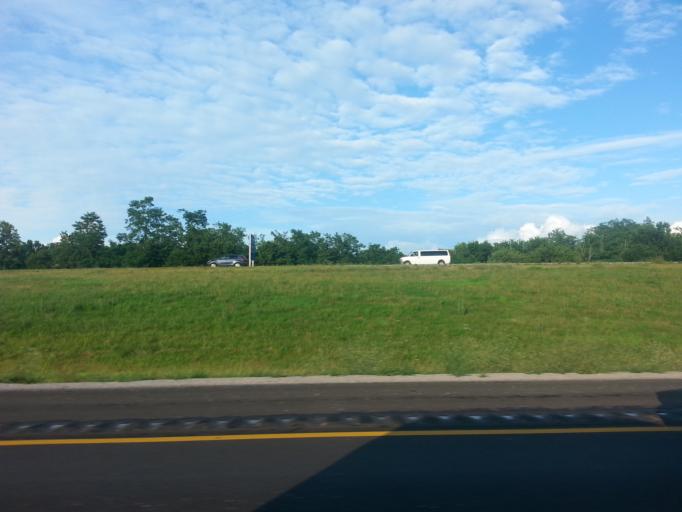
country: US
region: Kentucky
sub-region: Madison County
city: Richmond
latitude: 37.7131
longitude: -84.3207
